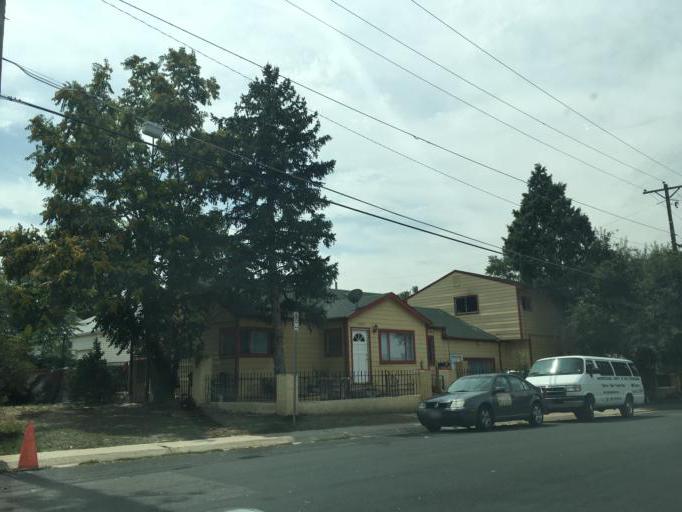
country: US
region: Colorado
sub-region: Adams County
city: Aurora
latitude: 39.7383
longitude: -104.8590
